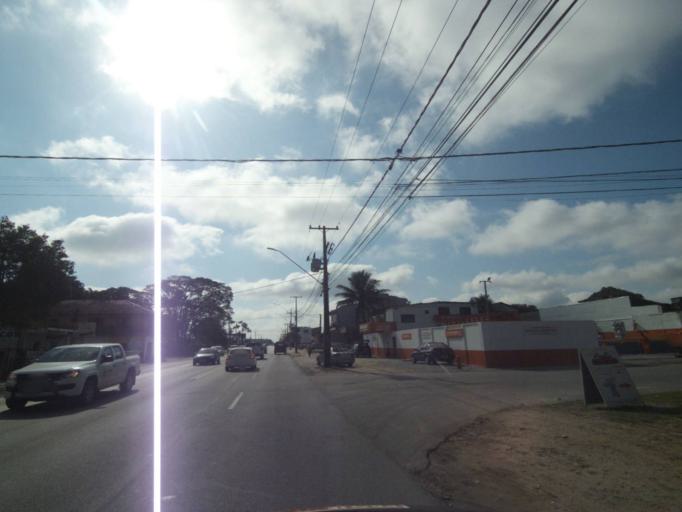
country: BR
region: Parana
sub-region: Paranagua
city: Paranagua
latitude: -25.5501
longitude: -48.5475
